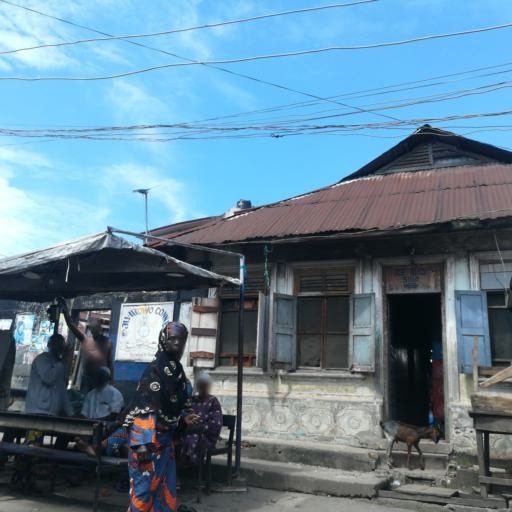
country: NG
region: Lagos
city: Lagos
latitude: 6.4639
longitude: 3.3908
